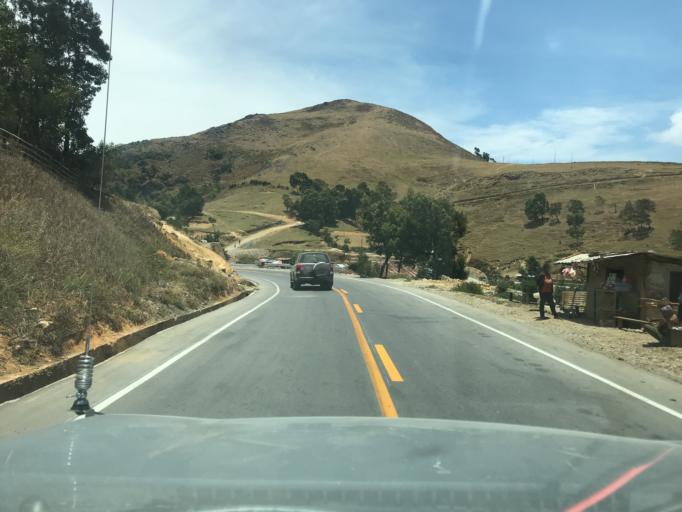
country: TL
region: Manufahi
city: Same
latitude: -8.8781
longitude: 125.6035
